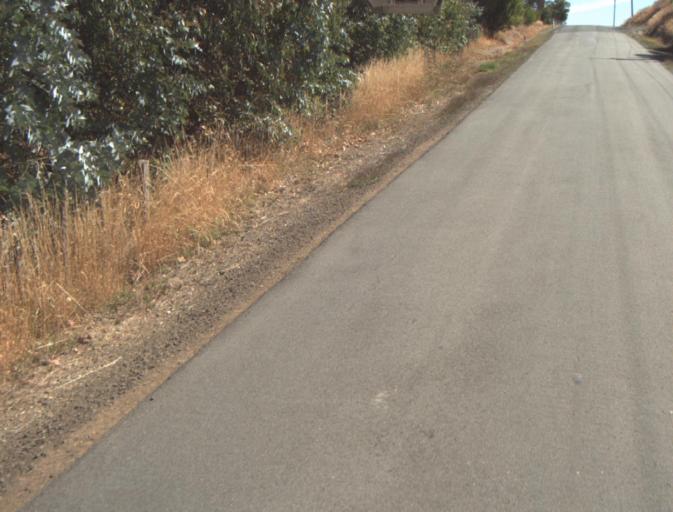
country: AU
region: Tasmania
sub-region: Launceston
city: Mayfield
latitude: -41.2352
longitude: 147.2345
